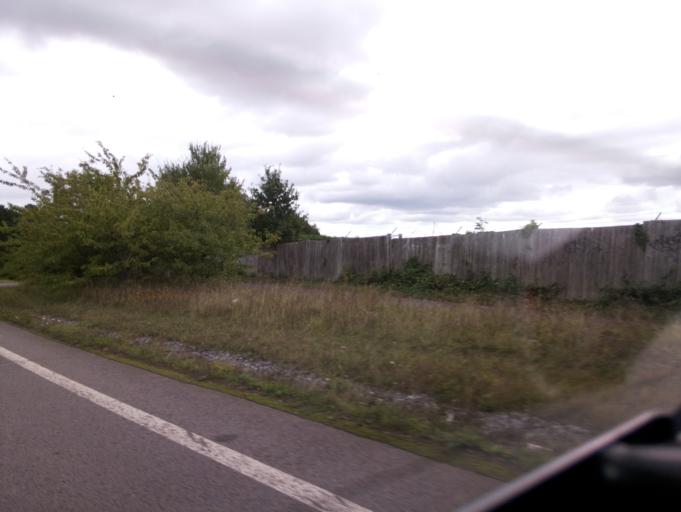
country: GB
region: England
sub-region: Devon
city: Heavitree
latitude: 50.7065
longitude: -3.4854
